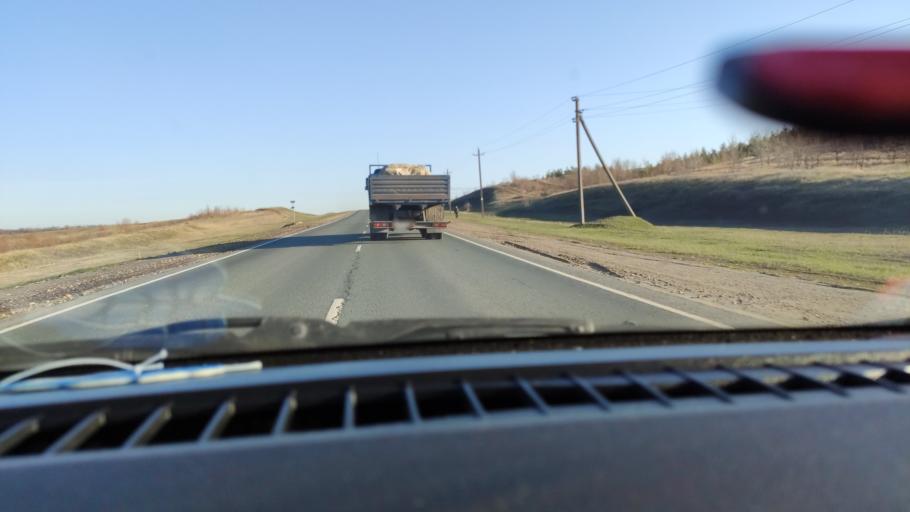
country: RU
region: Saratov
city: Alekseyevka
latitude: 52.2995
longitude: 47.9276
